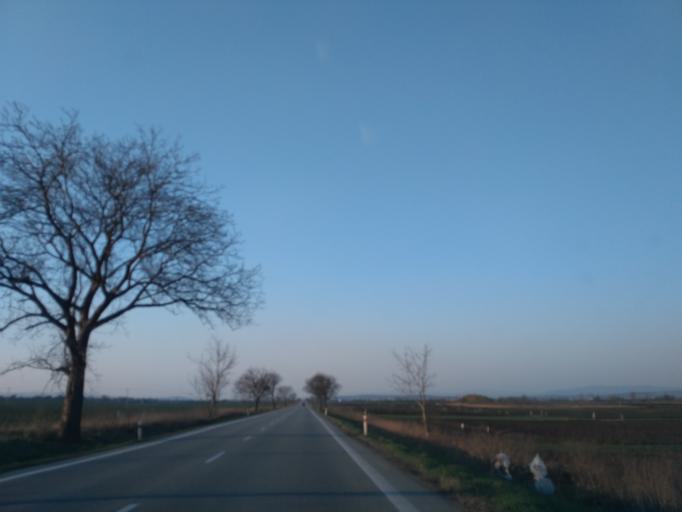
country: SK
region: Kosicky
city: Kosice
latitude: 48.6007
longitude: 21.2620
